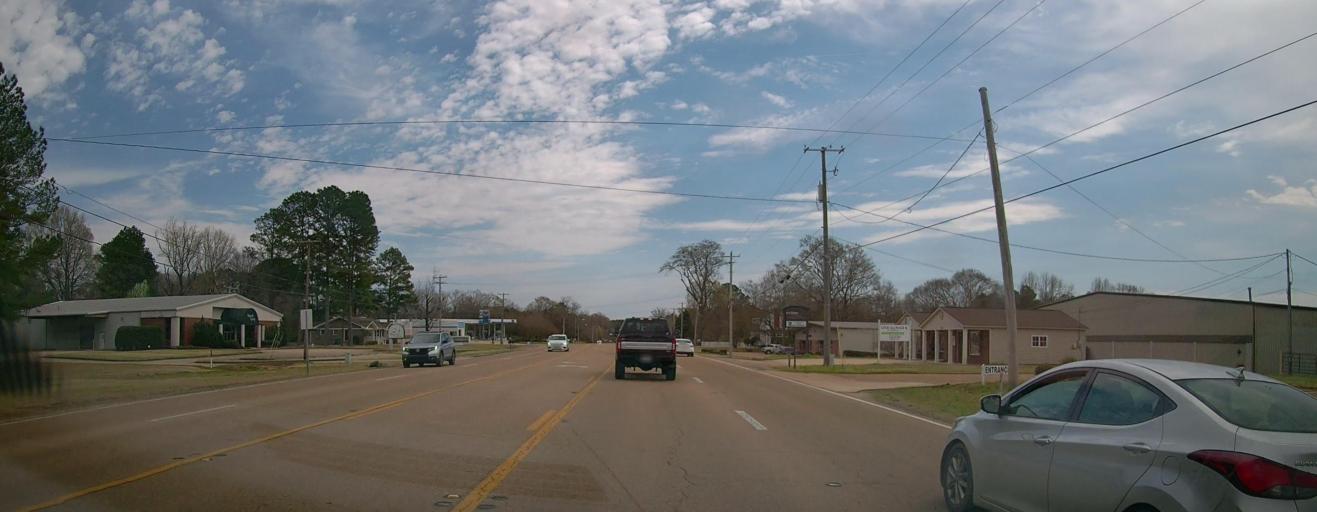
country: US
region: Mississippi
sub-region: Lee County
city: Tupelo
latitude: 34.2863
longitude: -88.7405
